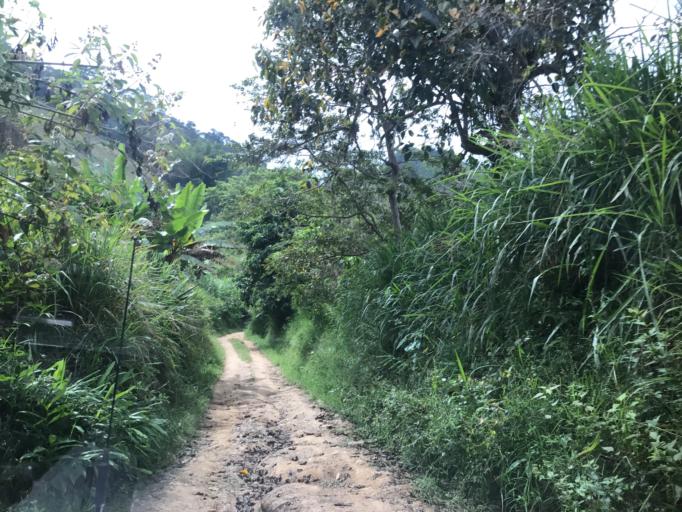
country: CO
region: Valle del Cauca
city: Obando
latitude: 4.5621
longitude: -75.8975
